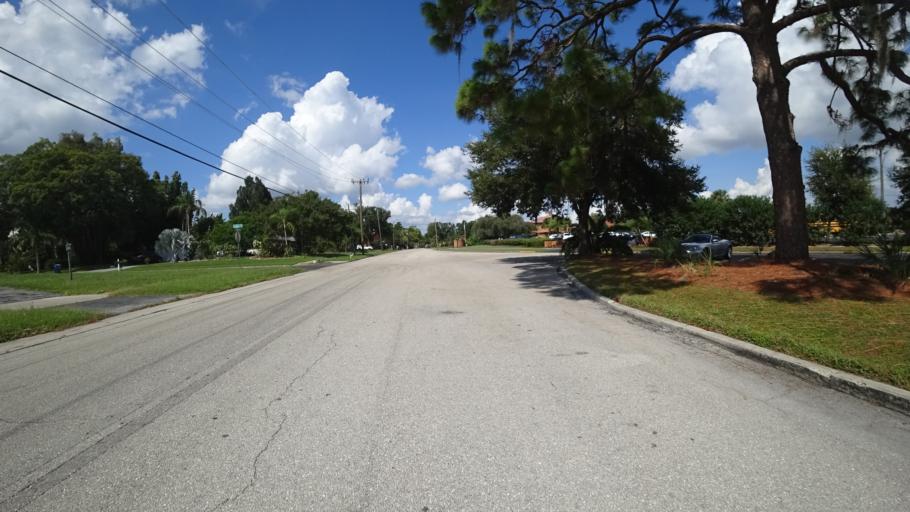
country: US
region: Florida
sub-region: Manatee County
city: Whitfield
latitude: 27.4142
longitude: -82.5673
